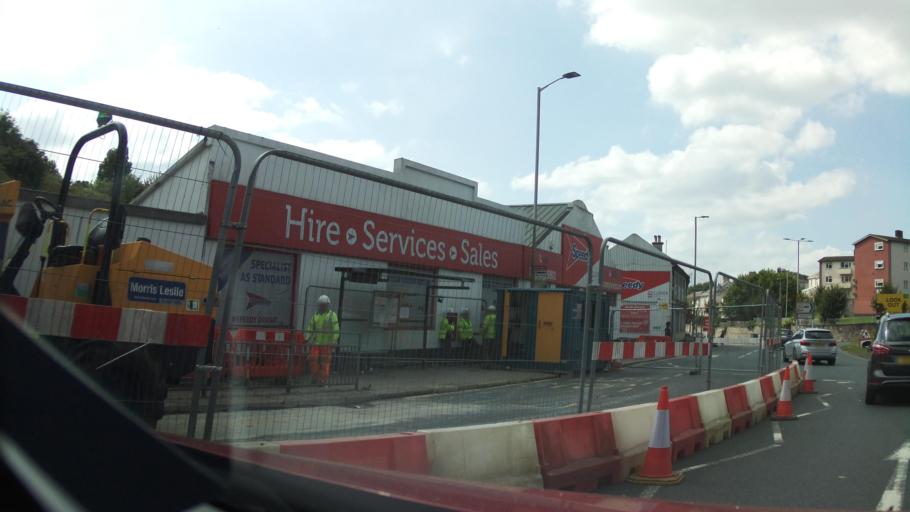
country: GB
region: England
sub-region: Plymouth
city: Plymouth
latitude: 50.3775
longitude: -4.1471
